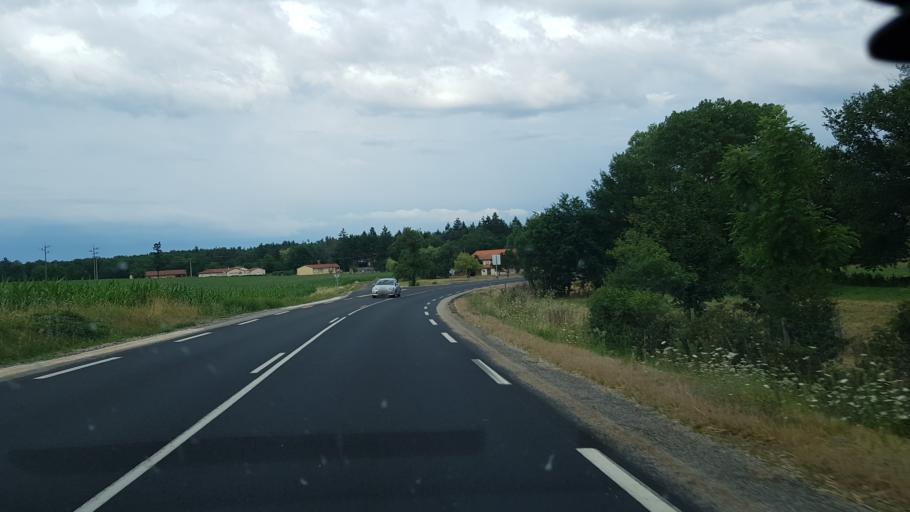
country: FR
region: Auvergne
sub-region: Departement de la Haute-Loire
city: Bournoncle-Saint-Pierre
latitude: 45.2741
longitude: 3.2957
